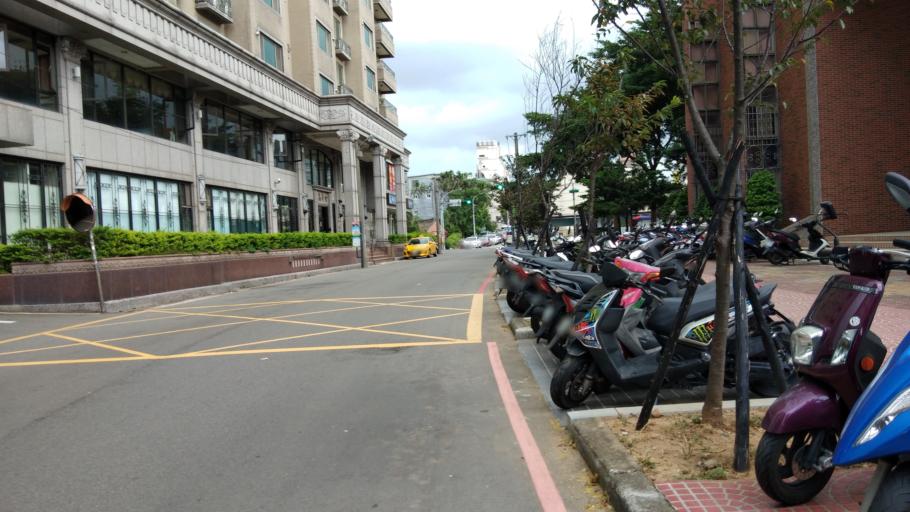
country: TW
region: Taiwan
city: Taoyuan City
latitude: 24.9595
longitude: 121.2047
